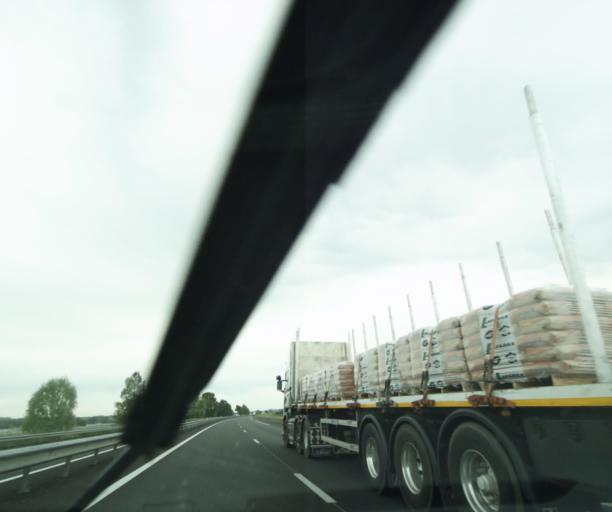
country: FR
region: Midi-Pyrenees
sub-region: Departement du Tarn-et-Garonne
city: Albias
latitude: 44.0928
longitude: 1.4291
